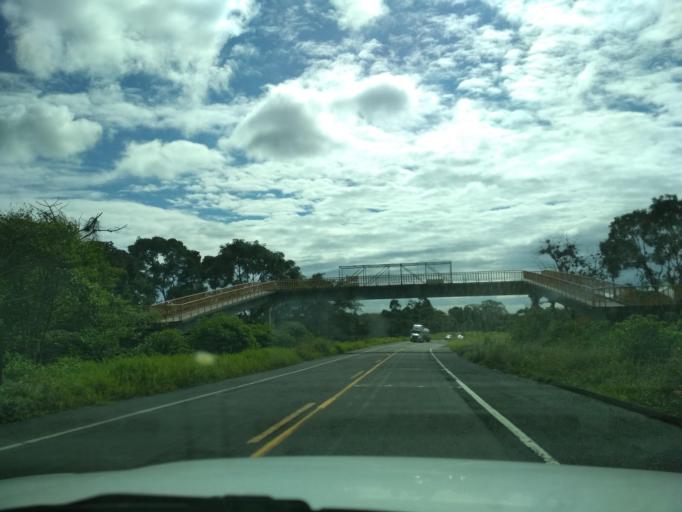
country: MX
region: Veracruz
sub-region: Coatepec
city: Las Lomas
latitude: 19.4532
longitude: -96.9294
